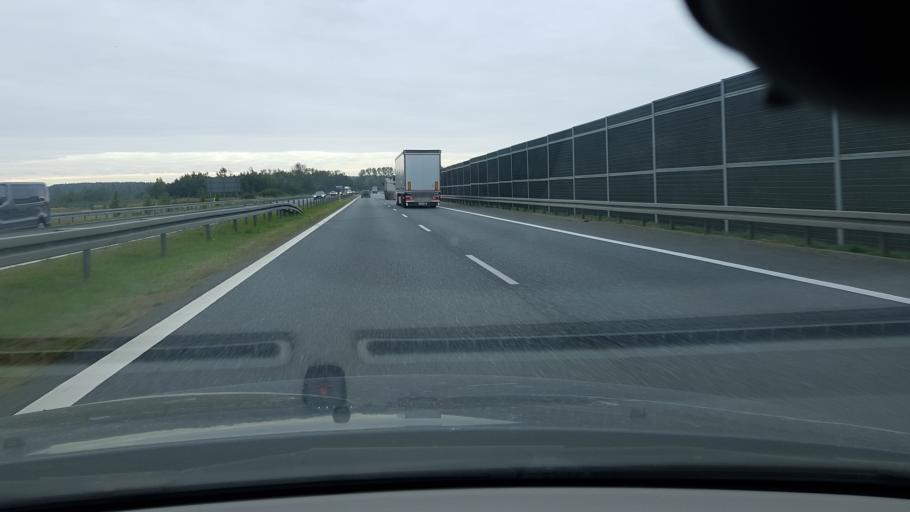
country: PL
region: Masovian Voivodeship
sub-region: Powiat zyrardowski
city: Mszczonow
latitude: 51.9641
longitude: 20.4999
